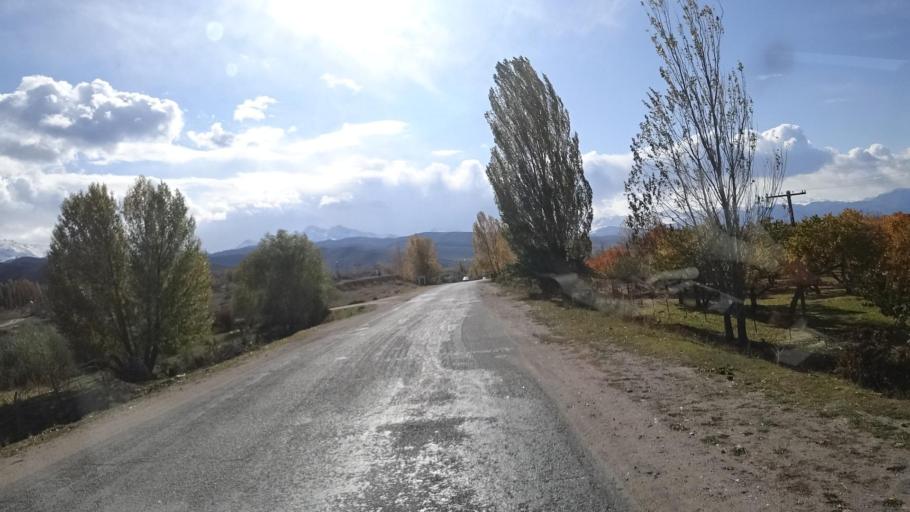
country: KG
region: Ysyk-Koel
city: Pokrovka
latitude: 42.2276
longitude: 77.7141
